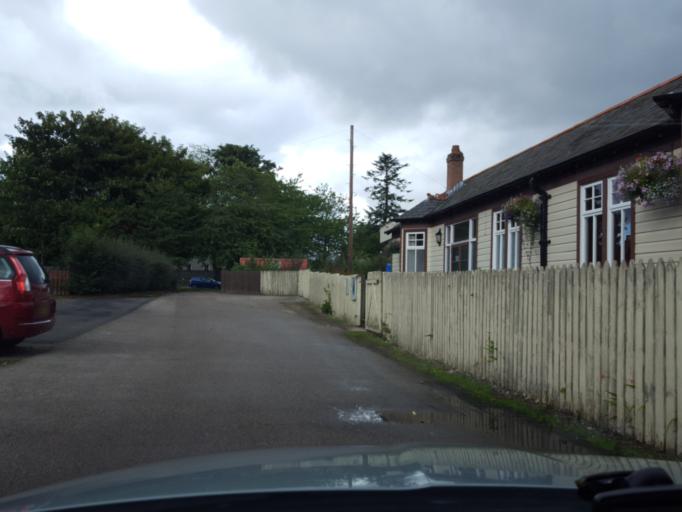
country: GB
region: Scotland
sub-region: Aberdeenshire
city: Alford
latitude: 57.2317
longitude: -2.6980
